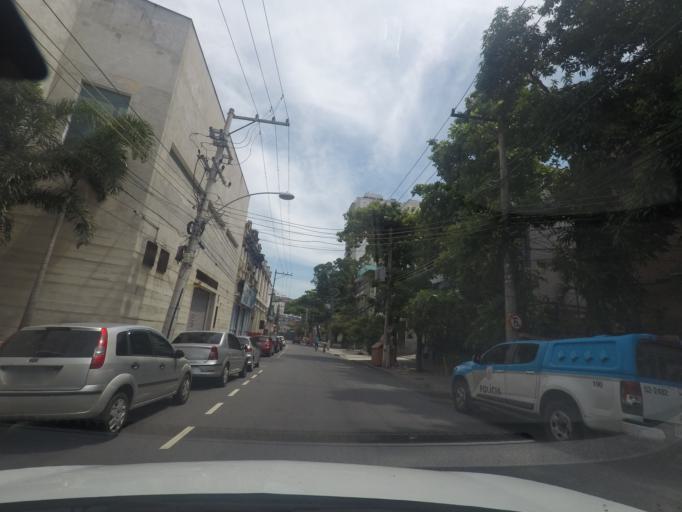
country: BR
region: Rio de Janeiro
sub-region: Rio De Janeiro
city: Rio de Janeiro
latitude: -22.9213
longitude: -43.2087
